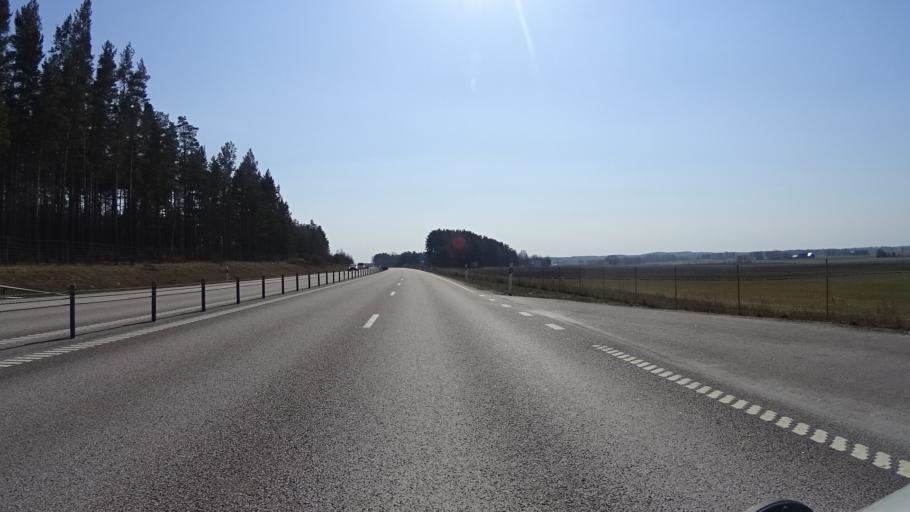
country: SE
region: OEstergoetland
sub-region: Mjolby Kommun
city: Mjolby
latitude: 58.3476
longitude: 15.1069
